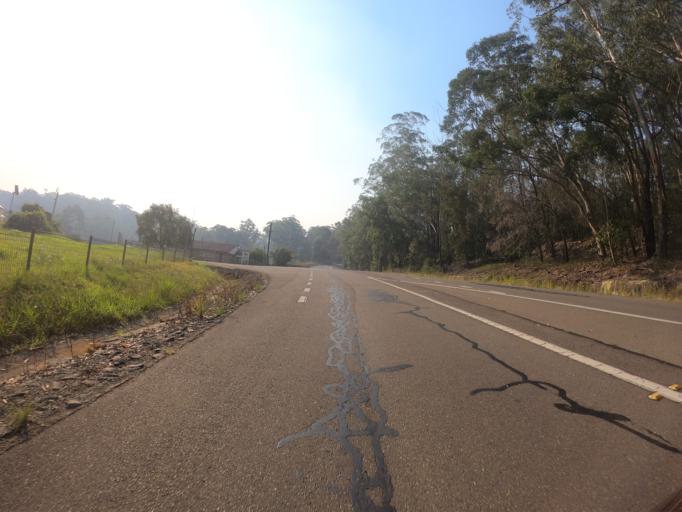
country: AU
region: New South Wales
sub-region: Wollondilly
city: Douglas Park
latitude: -34.2280
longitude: 150.7443
